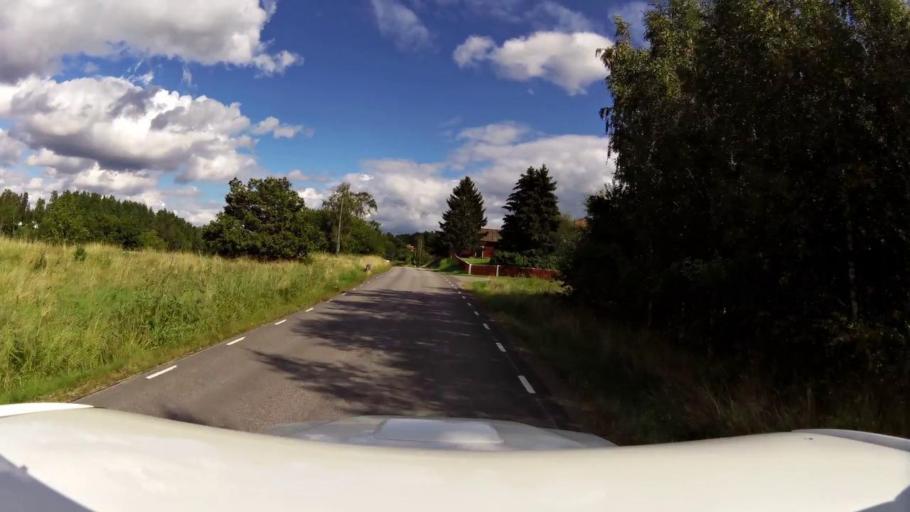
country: SE
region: OEstergoetland
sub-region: Kinda Kommun
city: Rimforsa
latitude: 58.2280
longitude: 15.7228
